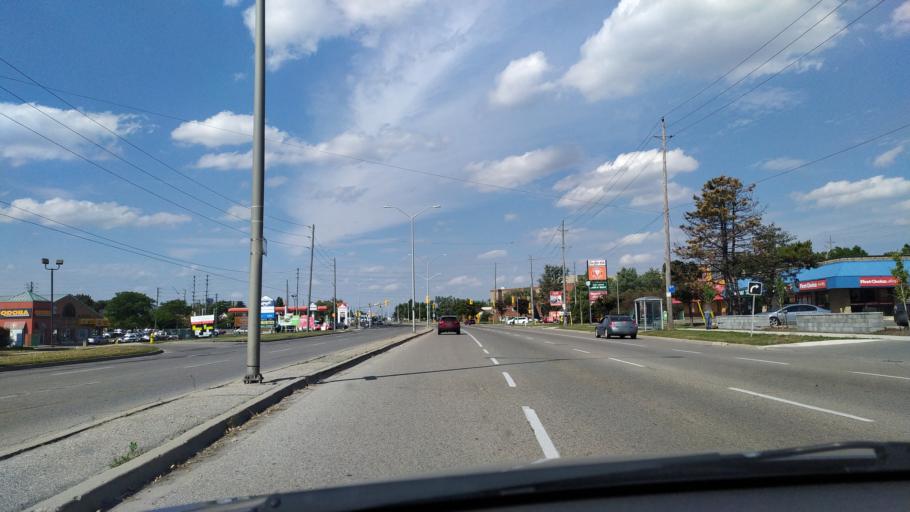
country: CA
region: Ontario
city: London
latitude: 42.9421
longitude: -81.2254
